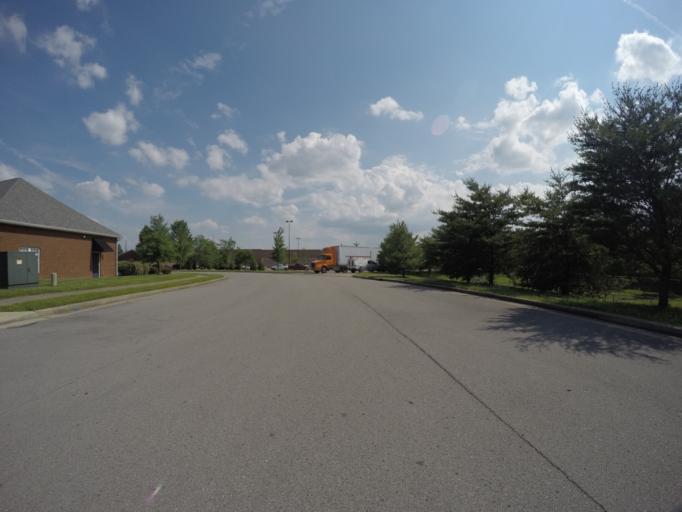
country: US
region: Tennessee
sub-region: Davidson County
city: Lakewood
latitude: 36.2186
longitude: -86.6008
